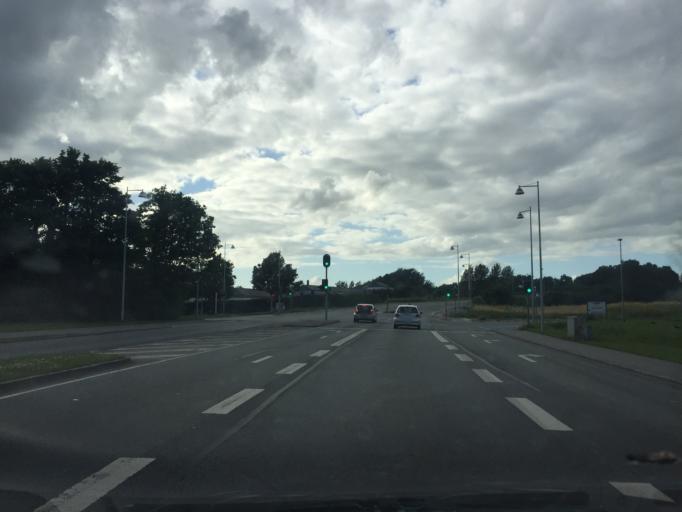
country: DK
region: Capital Region
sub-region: Albertslund Kommune
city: Albertslund
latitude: 55.6564
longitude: 12.3646
